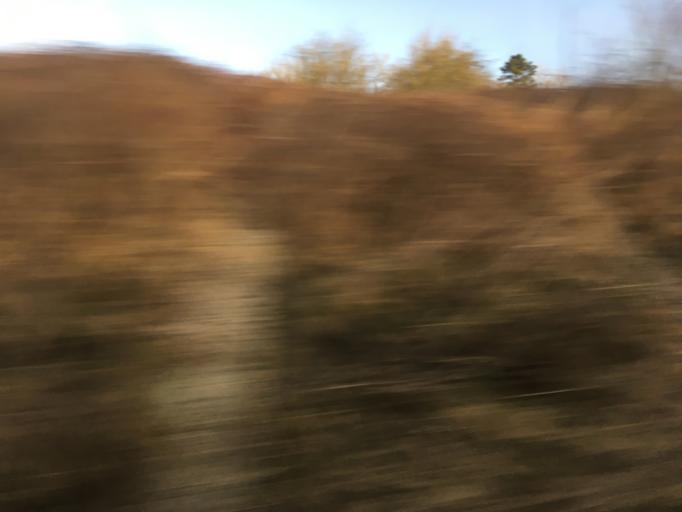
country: GB
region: England
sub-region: South Gloucestershire
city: Chipping Sodbury
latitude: 51.5320
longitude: -2.3664
